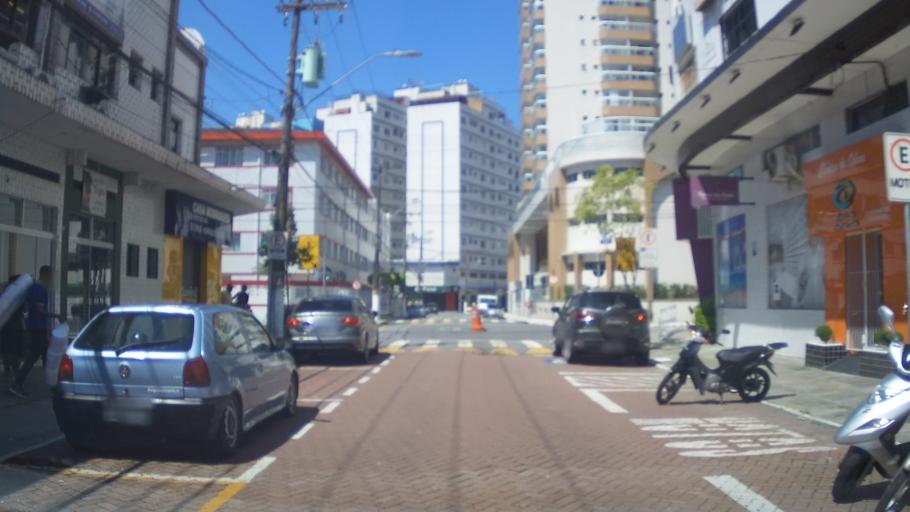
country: BR
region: Sao Paulo
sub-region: Praia Grande
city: Praia Grande
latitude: -24.0096
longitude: -46.4159
